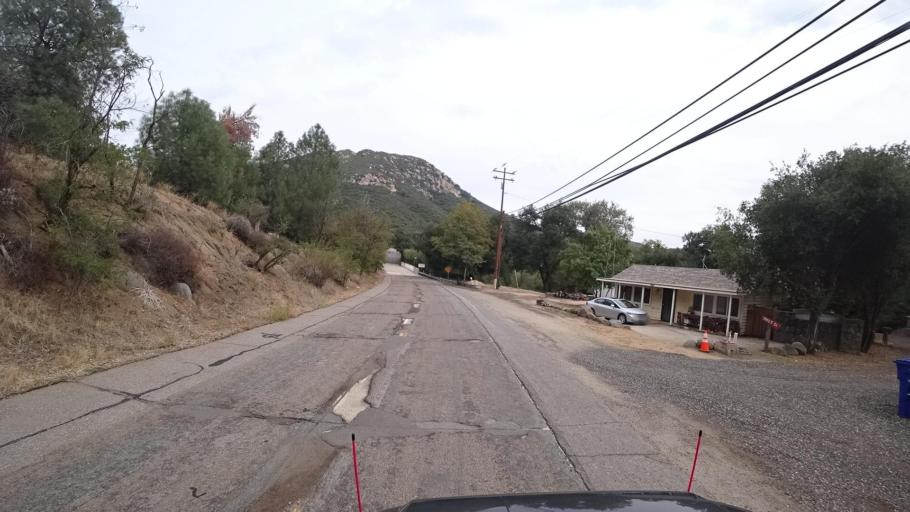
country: US
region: California
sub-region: San Diego County
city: Descanso
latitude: 32.8355
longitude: -116.6234
